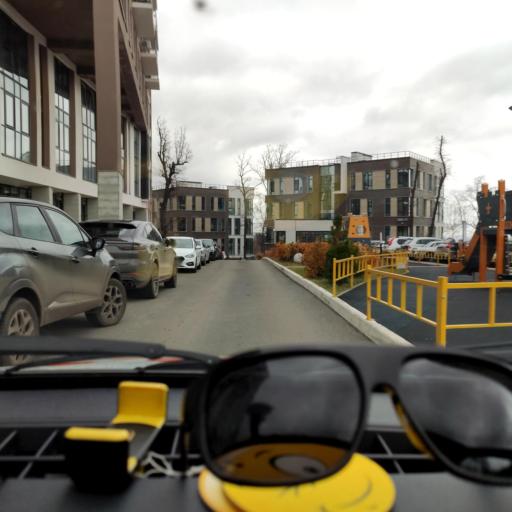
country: RU
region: Bashkortostan
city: Ufa
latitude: 54.7213
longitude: 56.0228
